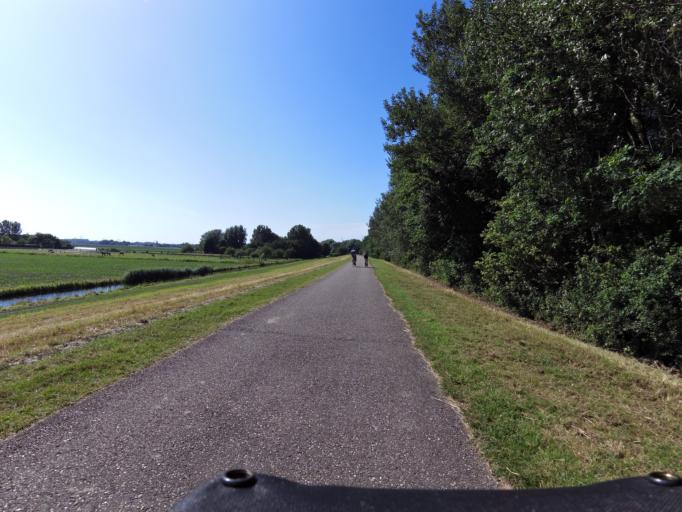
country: NL
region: South Holland
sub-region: Gemeente Brielle
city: Brielle
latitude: 51.9204
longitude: 4.1576
